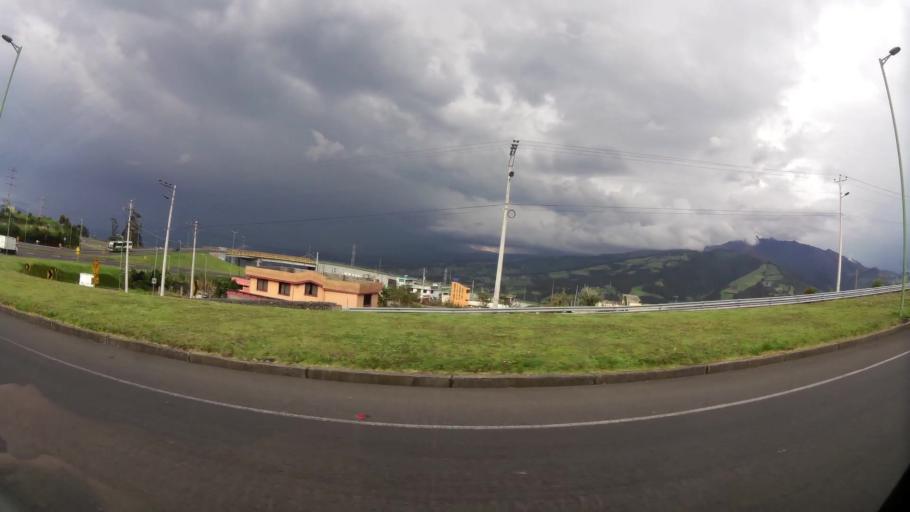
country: EC
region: Pichincha
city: Sangolqui
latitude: -0.3852
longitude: -78.5344
